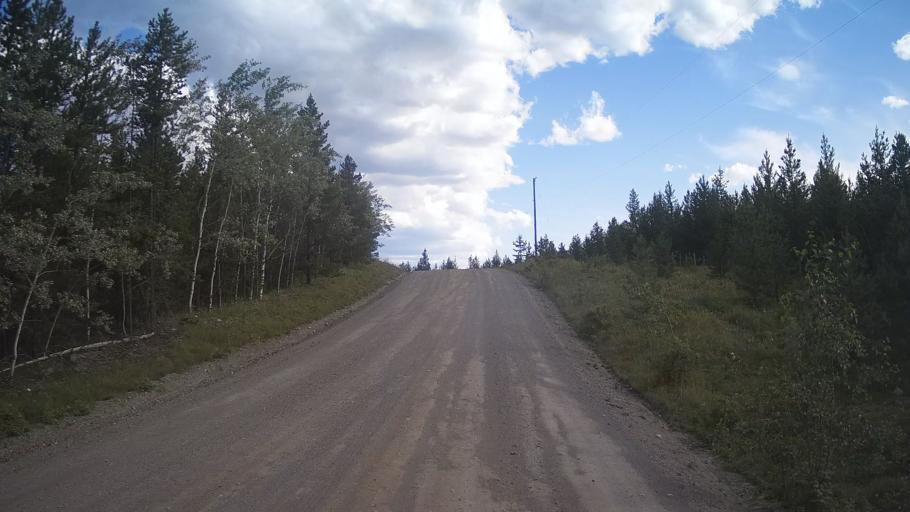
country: CA
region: British Columbia
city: Cache Creek
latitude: 51.2737
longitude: -121.7281
